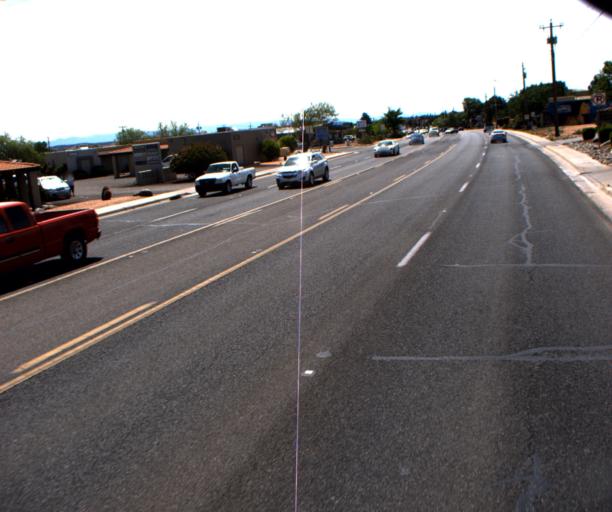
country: US
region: Arizona
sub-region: Yavapai County
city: Cottonwood
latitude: 34.7267
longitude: -112.0084
